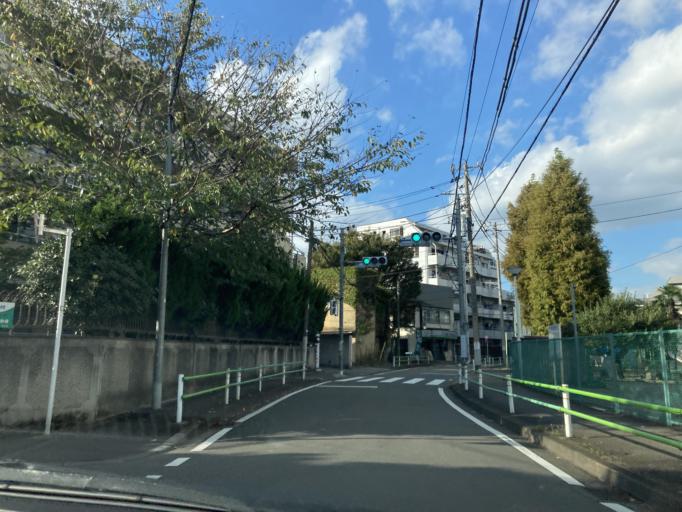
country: JP
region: Tokyo
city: Chofugaoka
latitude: 35.6463
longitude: 139.5561
